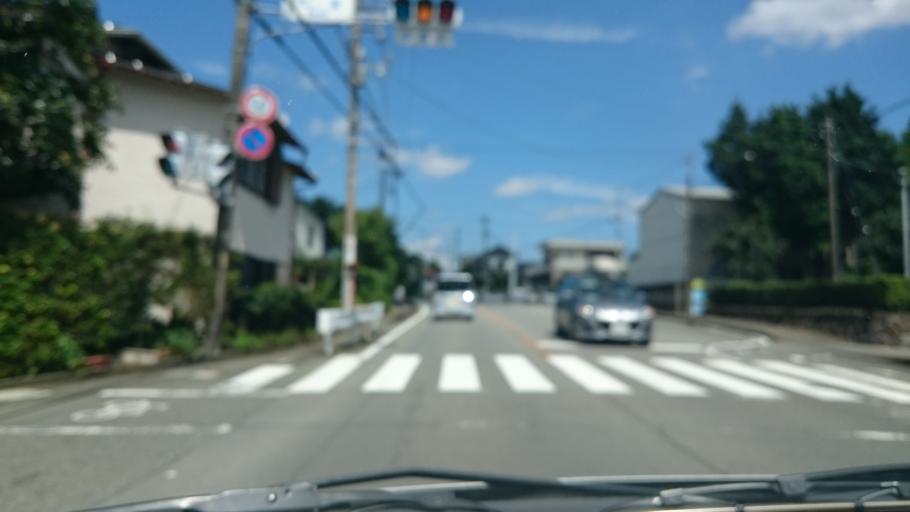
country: JP
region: Shizuoka
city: Gotemba
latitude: 35.2456
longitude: 138.9230
